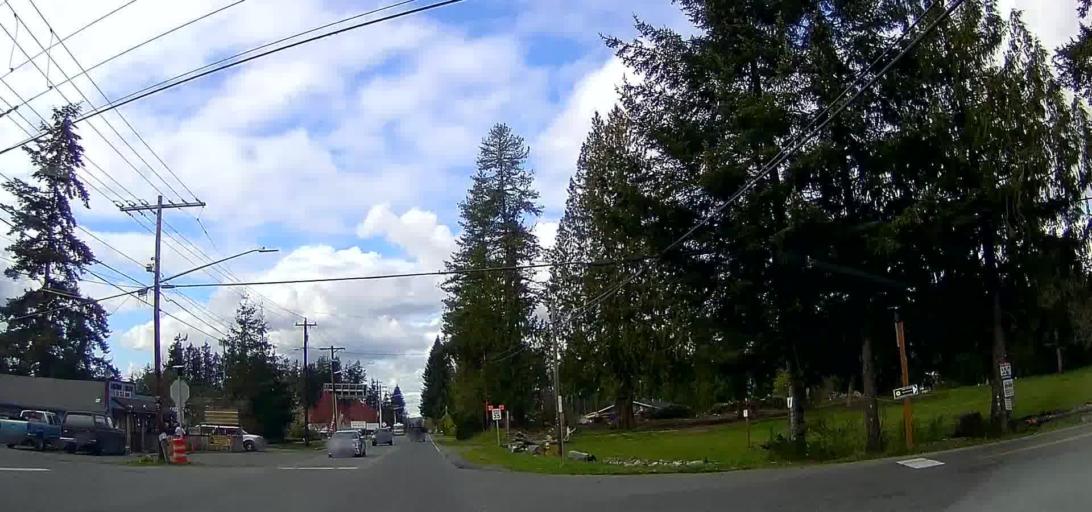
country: US
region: Washington
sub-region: Snohomish County
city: Smokey Point
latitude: 48.1670
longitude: -122.1855
